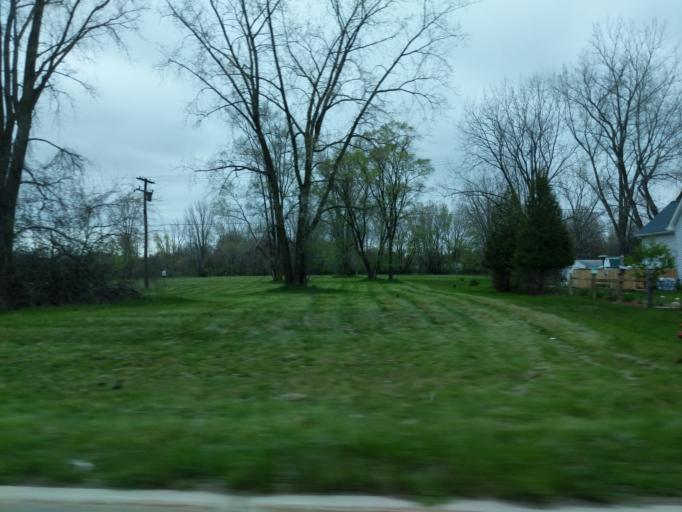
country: US
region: Michigan
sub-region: Tuscola County
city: Vassar
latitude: 43.3687
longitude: -83.5696
